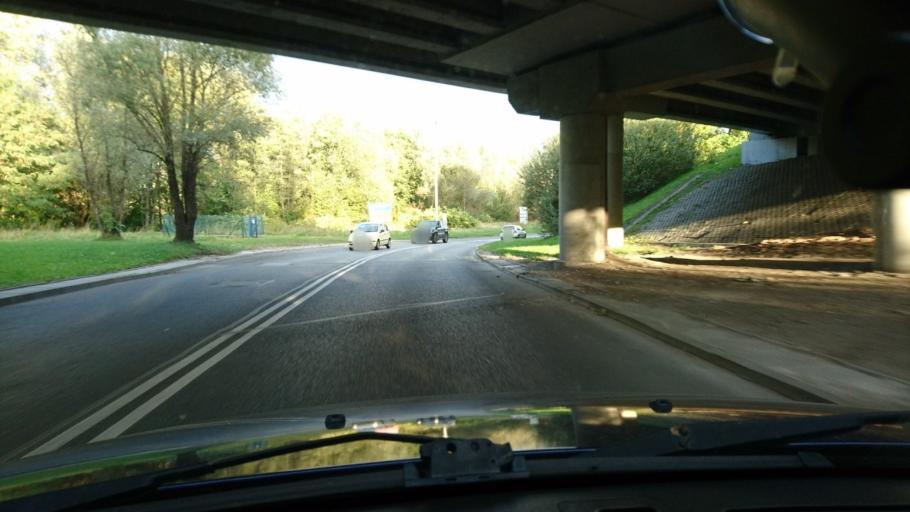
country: PL
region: Silesian Voivodeship
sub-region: Bielsko-Biala
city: Bielsko-Biala
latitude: 49.8099
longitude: 19.0271
